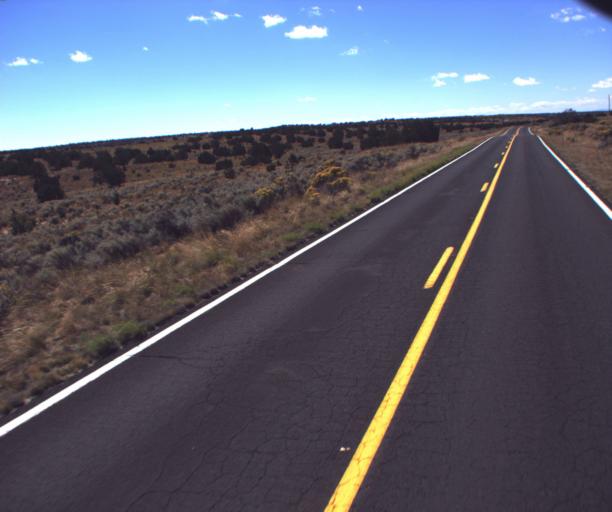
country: US
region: Arizona
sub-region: Apache County
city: Houck
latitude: 34.9447
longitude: -109.1751
